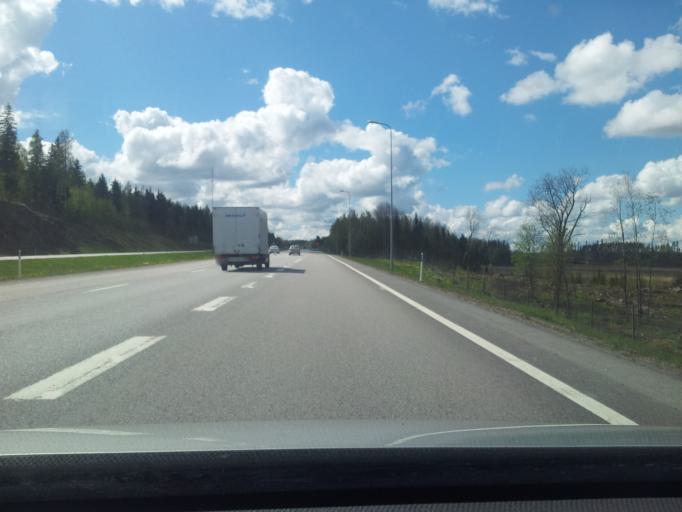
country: FI
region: Uusimaa
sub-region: Loviisa
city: Perna
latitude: 60.4851
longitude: 25.8874
